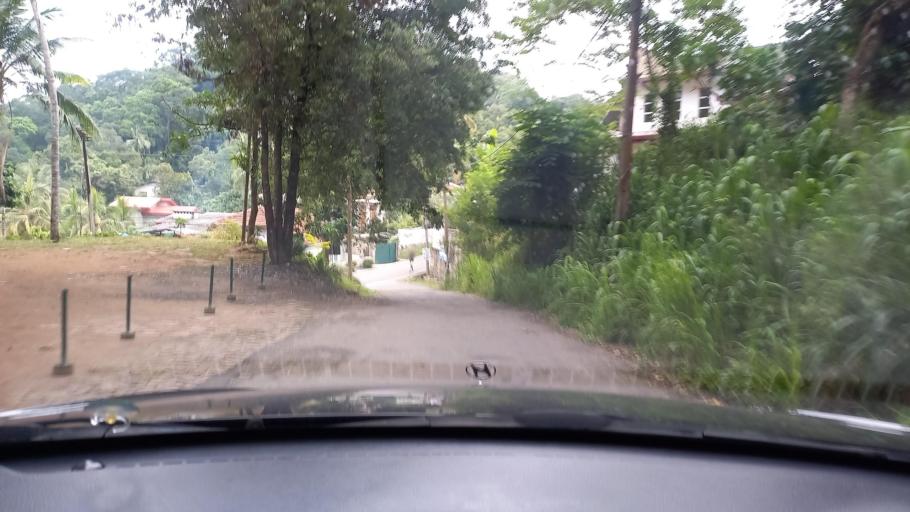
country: LK
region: Central
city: Kadugannawa
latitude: 7.2598
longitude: 80.3563
